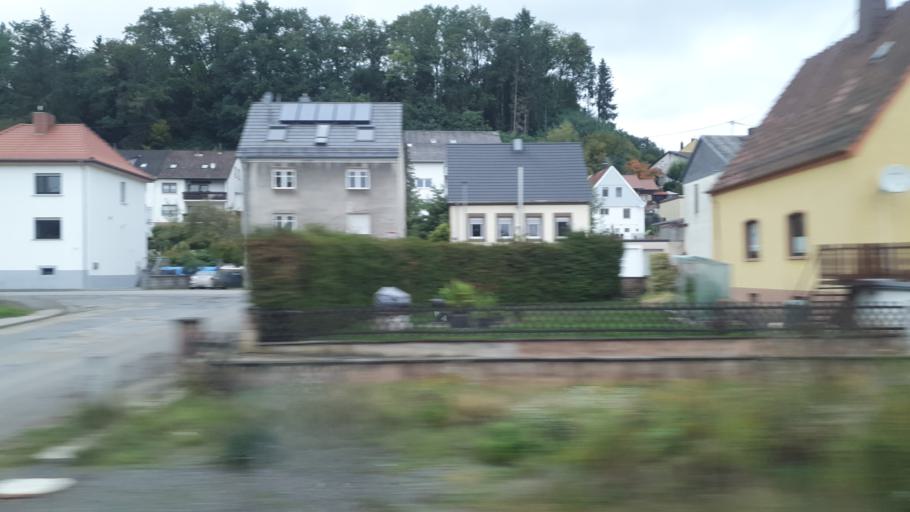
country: DE
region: Saarland
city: Blieskastel
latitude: 49.2662
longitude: 7.2933
